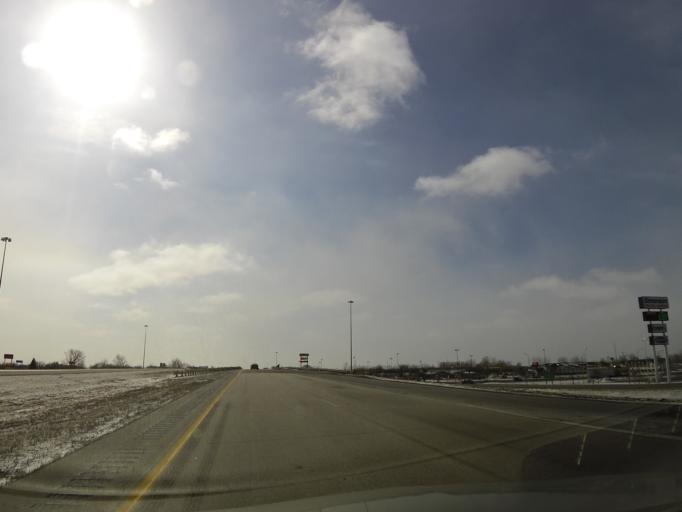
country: US
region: North Dakota
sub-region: Grand Forks County
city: Grand Forks
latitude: 47.9350
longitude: -97.0937
